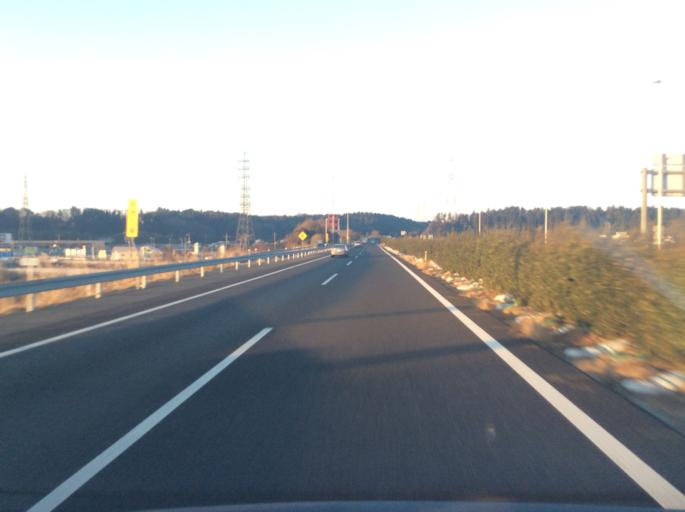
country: JP
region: Ibaraki
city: Mito-shi
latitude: 36.4178
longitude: 140.4264
